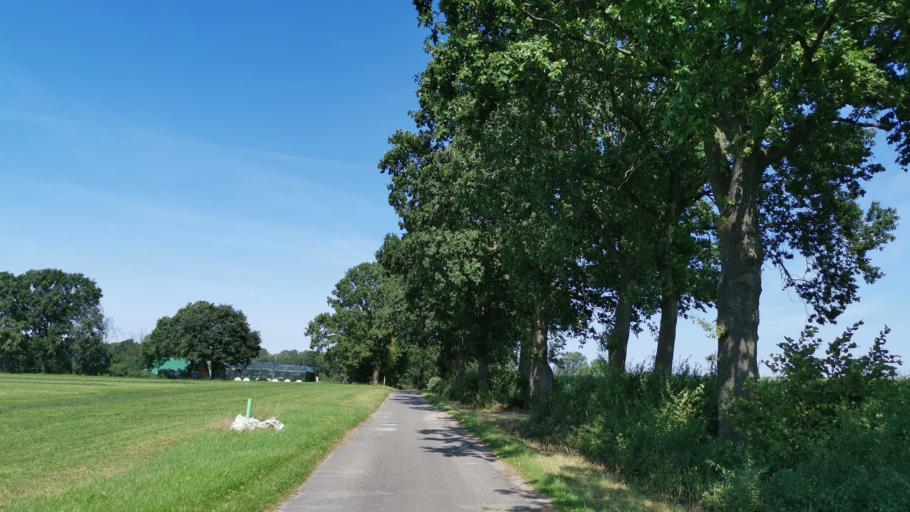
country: DE
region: Schleswig-Holstein
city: Gudow
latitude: 53.5726
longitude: 10.7694
